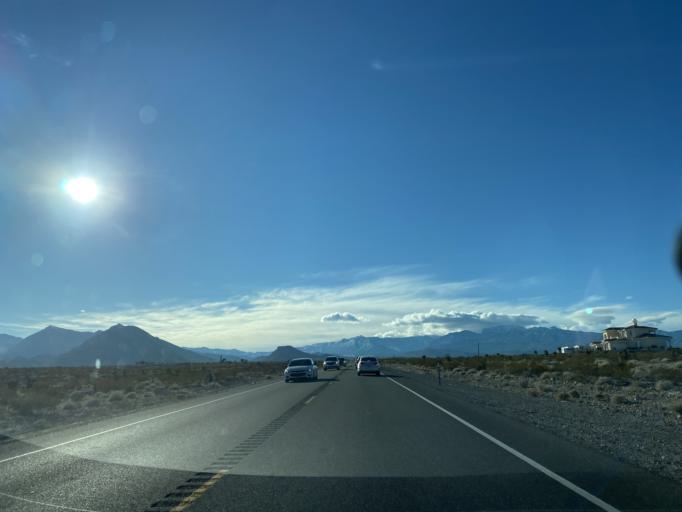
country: US
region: Nevada
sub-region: Clark County
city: Summerlin South
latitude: 36.3240
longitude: -115.3460
